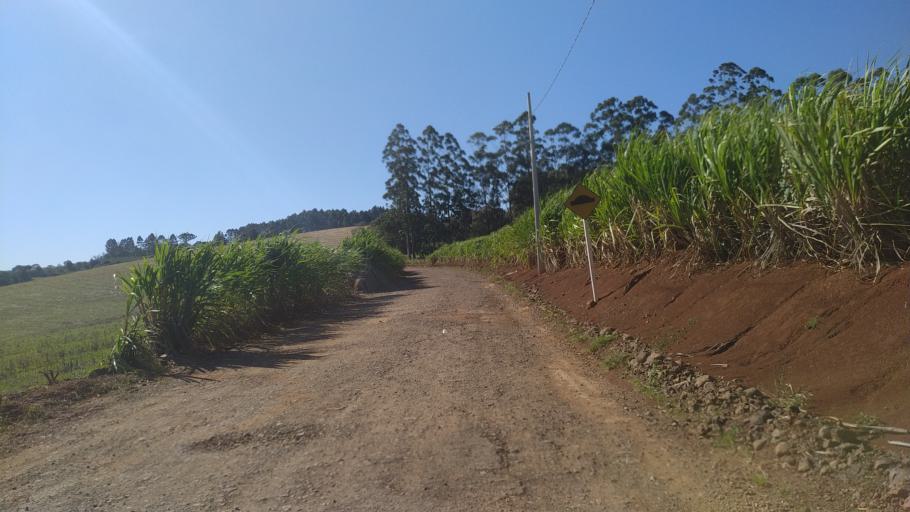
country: BR
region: Santa Catarina
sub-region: Chapeco
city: Chapeco
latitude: -27.1495
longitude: -52.6124
